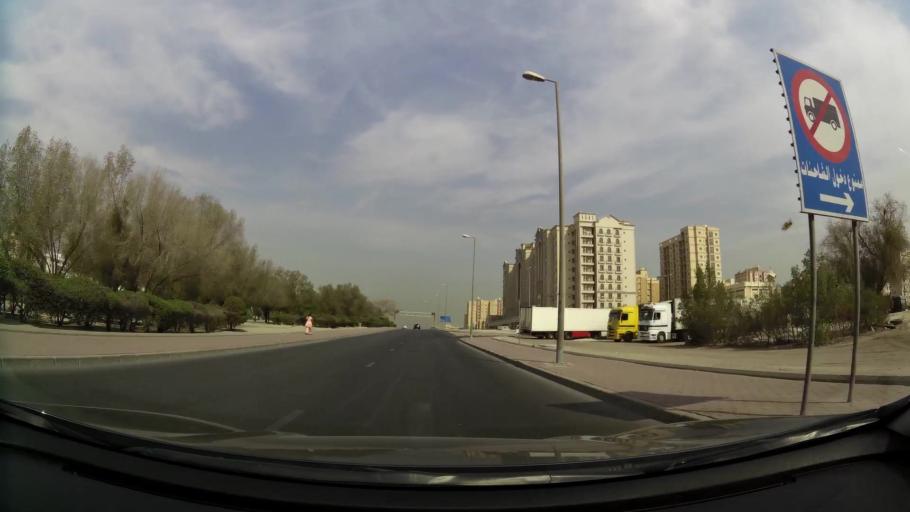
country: KW
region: Al Farwaniyah
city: Janub as Surrah
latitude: 29.2742
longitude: 47.9697
